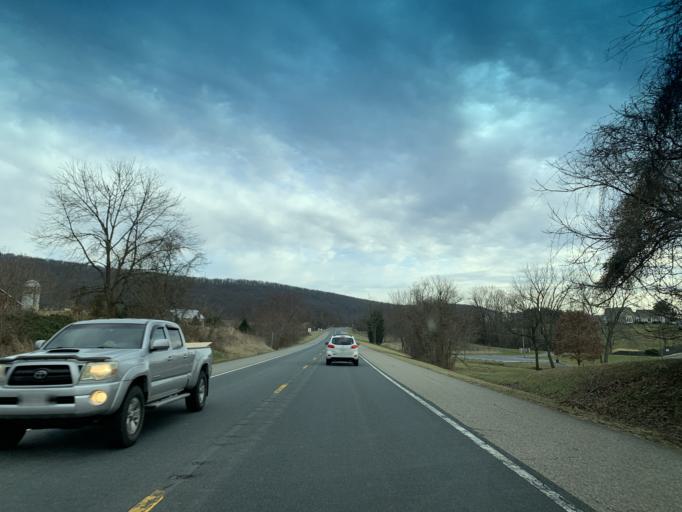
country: US
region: Maryland
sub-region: Frederick County
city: Brunswick
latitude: 39.4028
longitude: -77.6577
